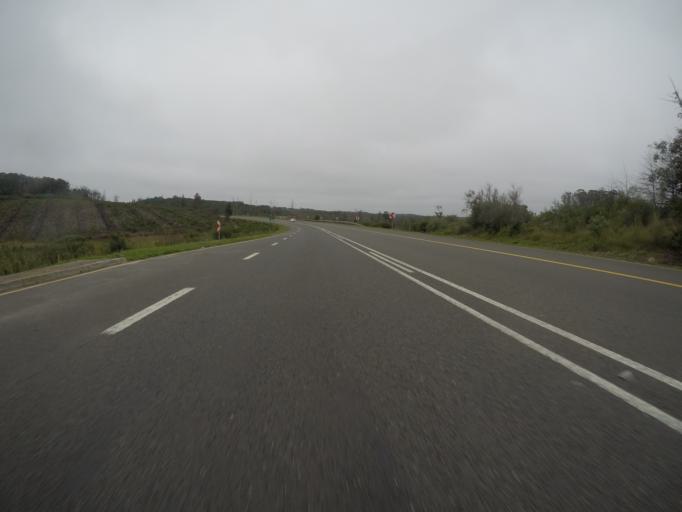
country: ZA
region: Western Cape
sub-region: Eden District Municipality
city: Knysna
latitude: -34.0362
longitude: 23.1548
